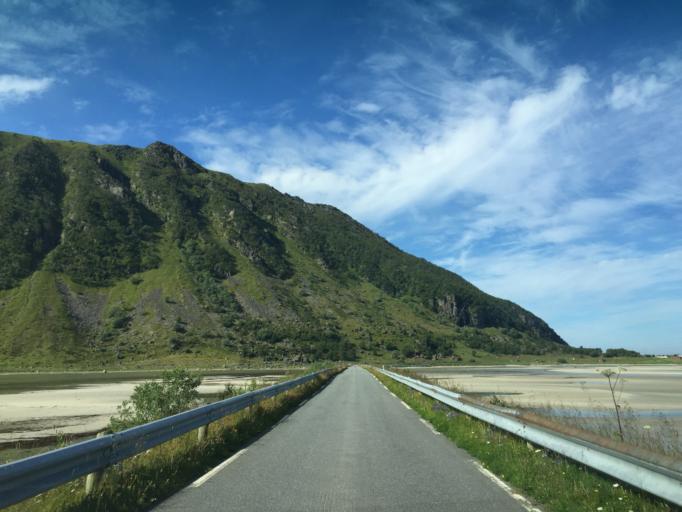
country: NO
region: Nordland
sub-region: Vagan
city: Svolvaer
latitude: 68.3949
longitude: 14.5506
